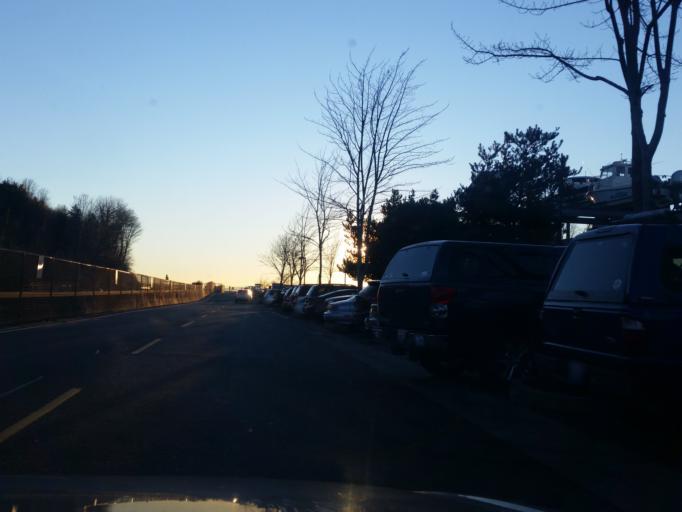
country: US
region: Washington
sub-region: Snohomish County
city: Woodway
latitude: 47.8056
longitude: -122.3920
